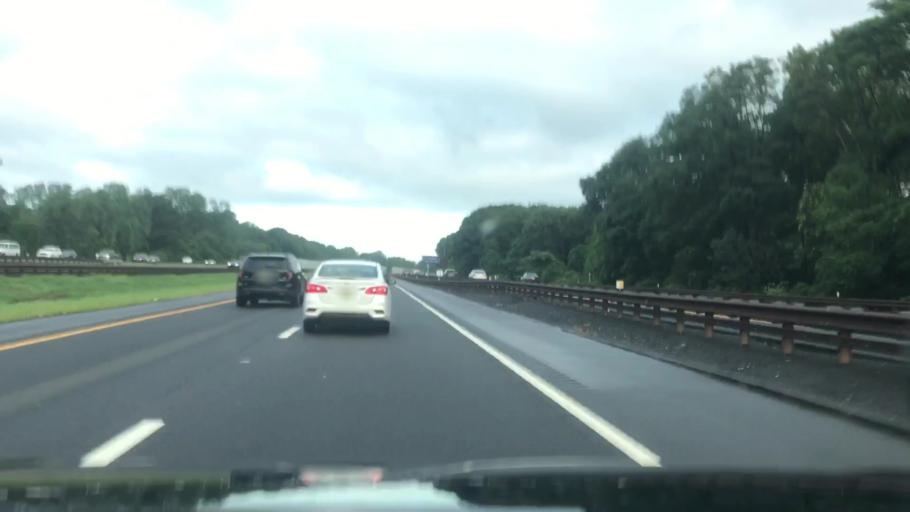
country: US
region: New Jersey
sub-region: Monmouth County
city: Lincroft
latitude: 40.3436
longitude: -74.1066
